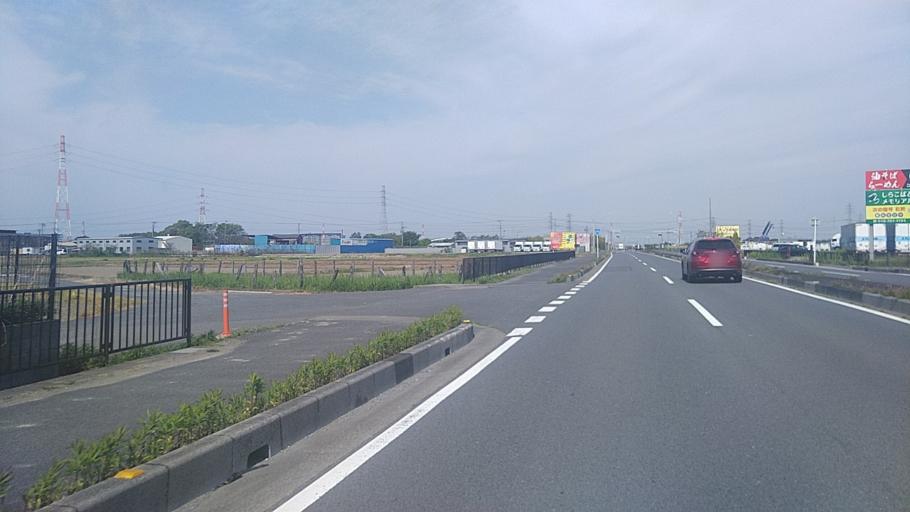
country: JP
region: Saitama
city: Koshigaya
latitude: 35.8981
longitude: 139.7549
